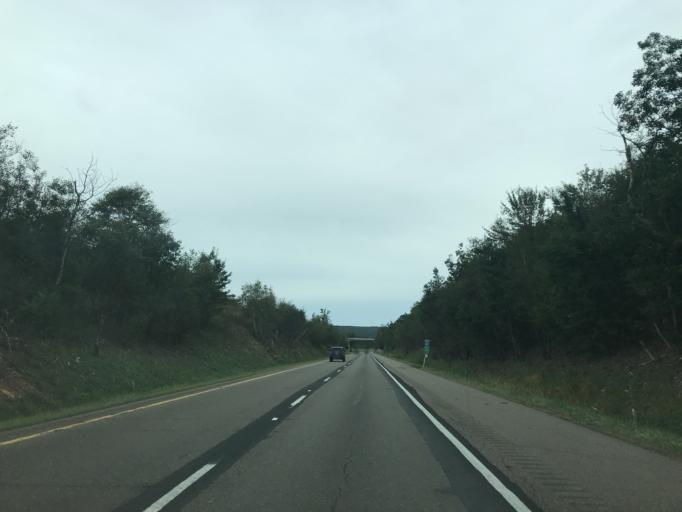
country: US
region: Pennsylvania
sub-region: Schuylkill County
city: McAdoo
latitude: 40.8608
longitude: -76.0414
